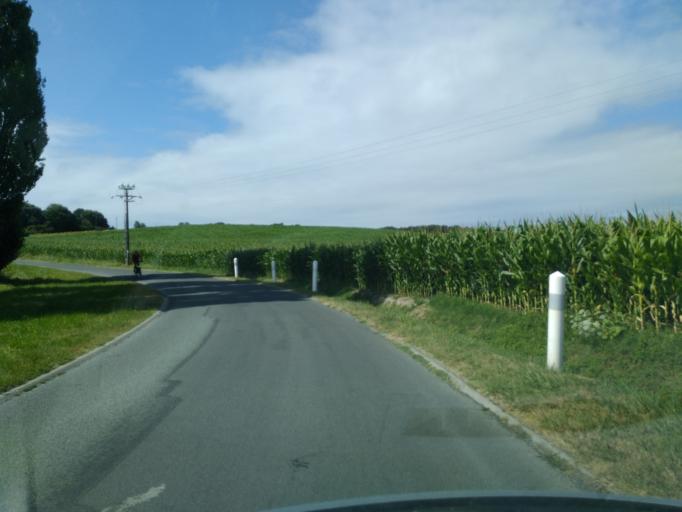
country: FR
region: Poitou-Charentes
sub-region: Departement de la Charente-Maritime
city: Saint-Palais-sur-Mer
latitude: 45.6791
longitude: -1.0868
